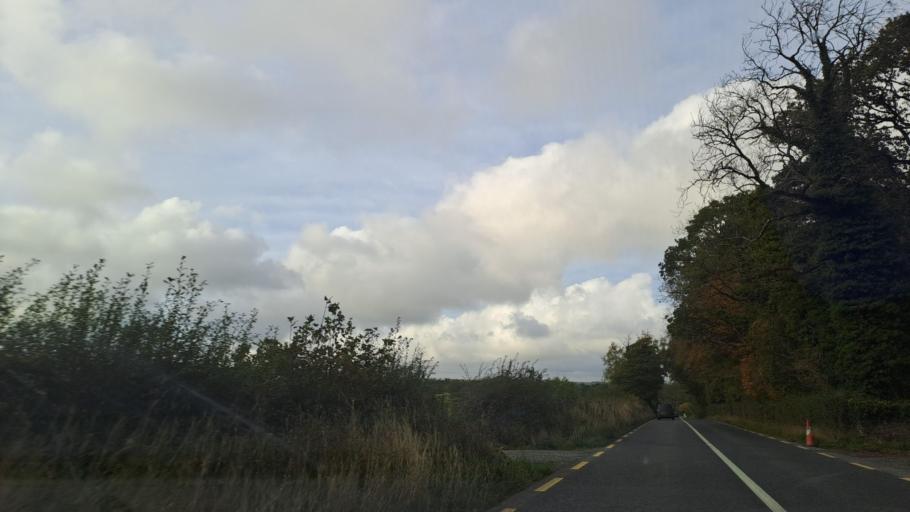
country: IE
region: Ulster
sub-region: An Cabhan
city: Kingscourt
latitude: 53.8546
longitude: -6.7808
